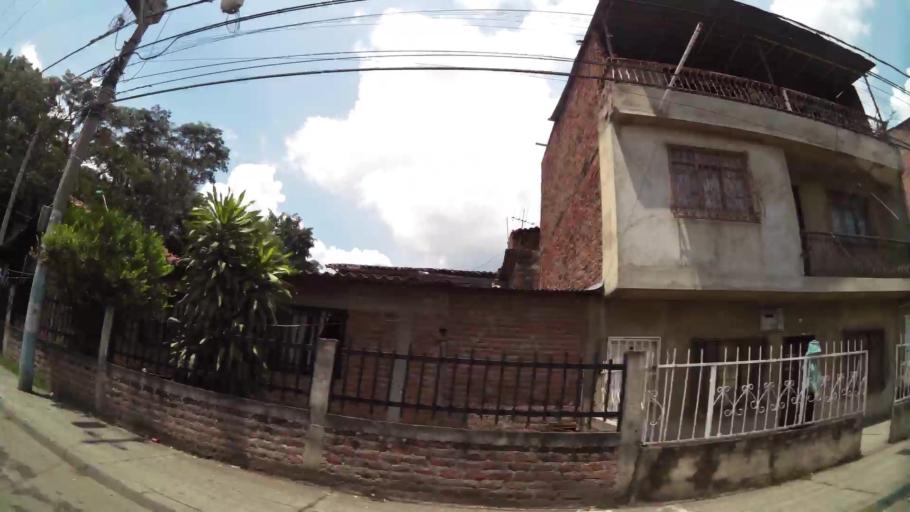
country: CO
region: Valle del Cauca
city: Cali
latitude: 3.4489
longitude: -76.4787
